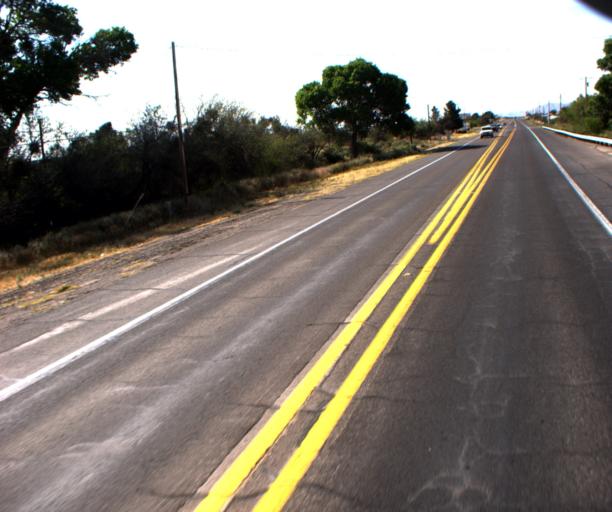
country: US
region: Arizona
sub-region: Graham County
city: Cactus Flat
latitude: 32.7619
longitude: -109.7164
